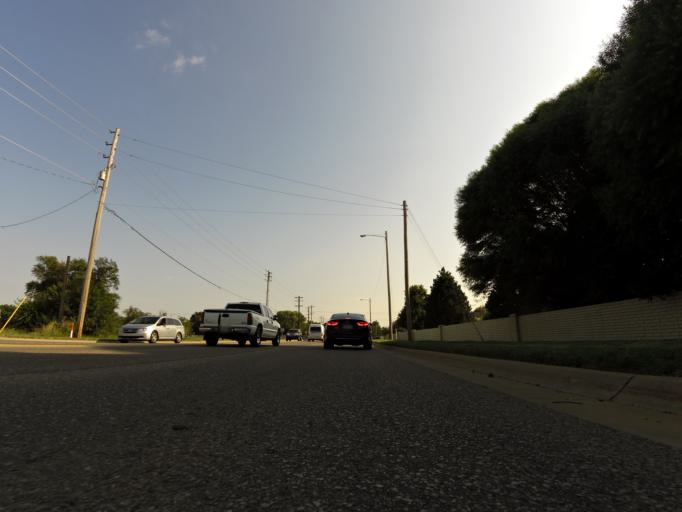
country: US
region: Kansas
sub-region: Sedgwick County
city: Maize
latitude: 37.7394
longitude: -97.4263
